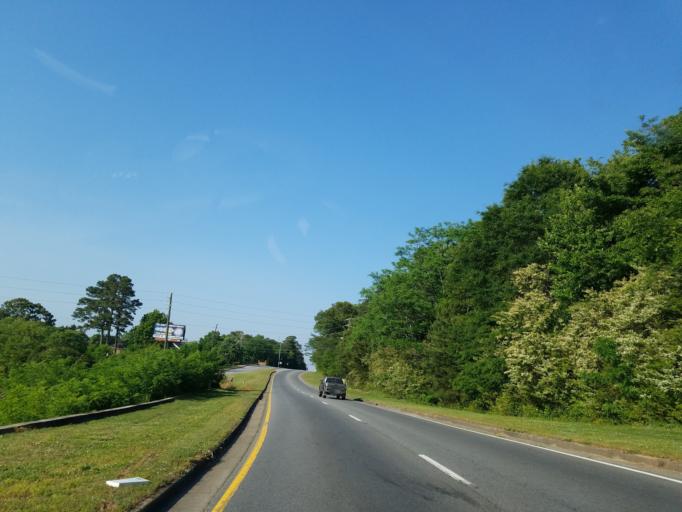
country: US
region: Georgia
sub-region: Forsyth County
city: Cumming
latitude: 34.2058
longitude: -84.1317
